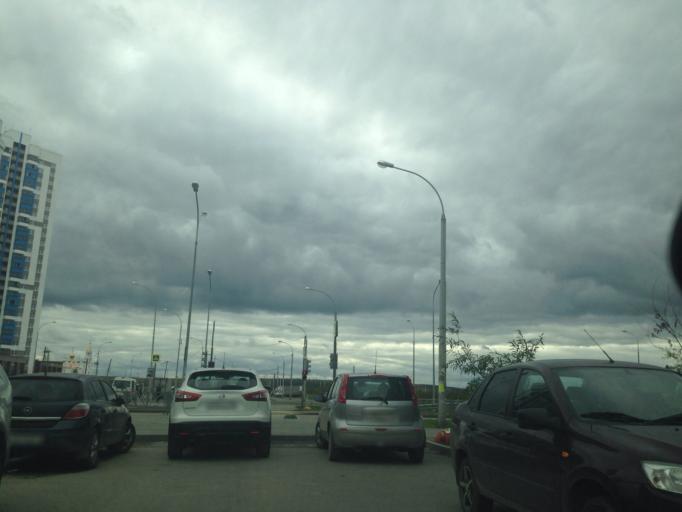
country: RU
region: Sverdlovsk
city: Shirokaya Rechka
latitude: 56.7899
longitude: 60.5151
